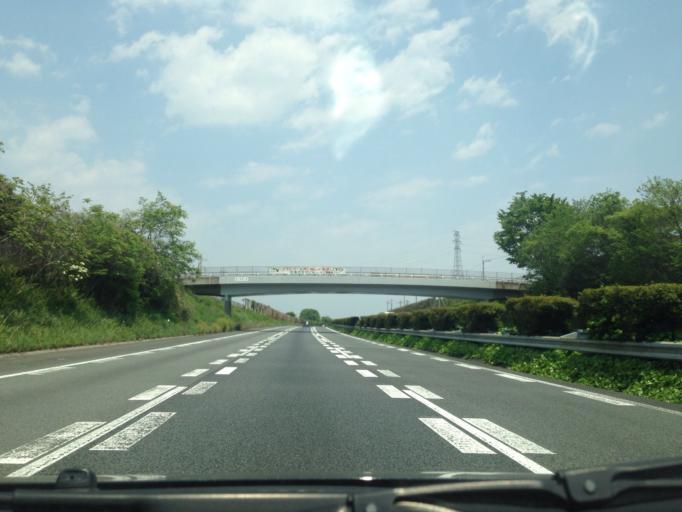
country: JP
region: Tochigi
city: Kanuma
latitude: 36.5177
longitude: 139.7746
